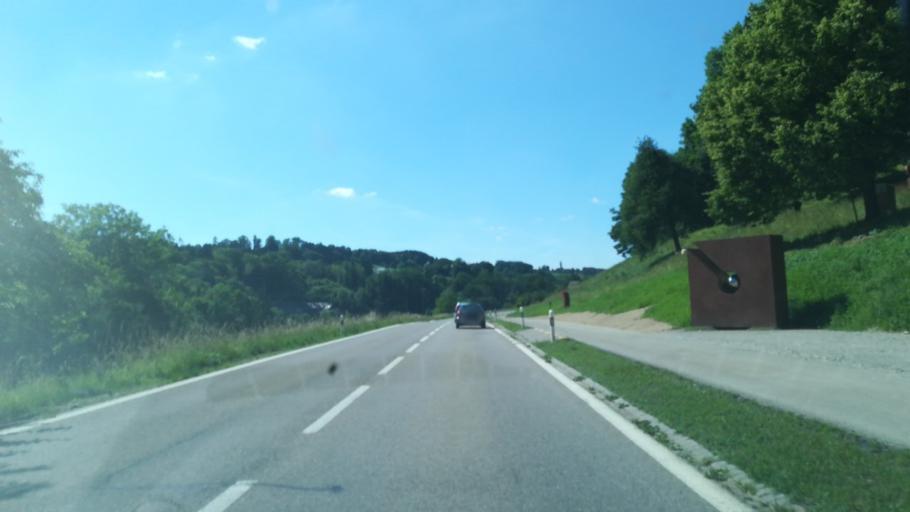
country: CH
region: Saint Gallen
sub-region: Wahlkreis Wil
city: Niederburen
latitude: 47.4987
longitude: 9.2183
